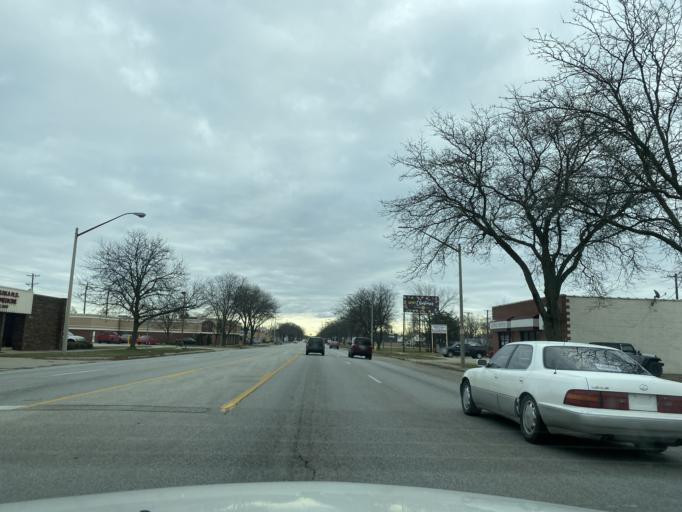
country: US
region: Michigan
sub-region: Wayne County
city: Southgate
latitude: 42.1996
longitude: -83.1726
